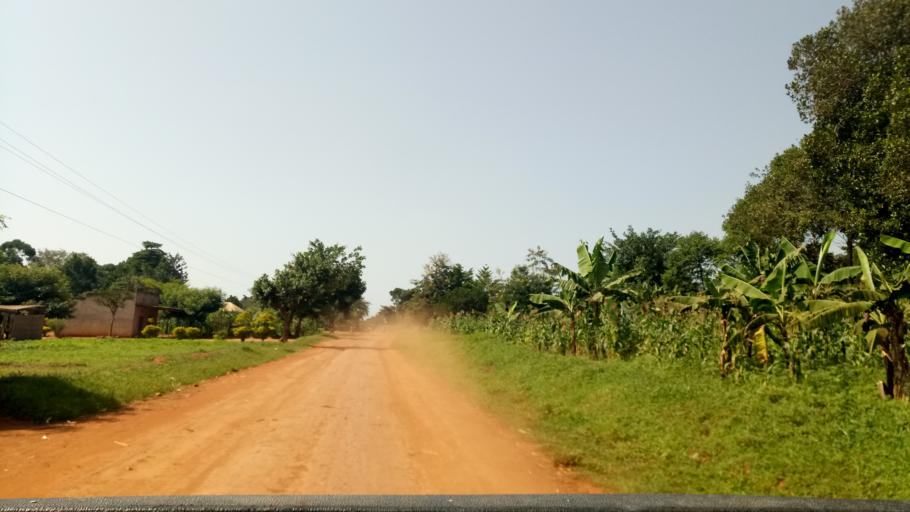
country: UG
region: Eastern Region
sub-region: Kaliro District
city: Kaliro
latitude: 0.9645
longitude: 33.4681
